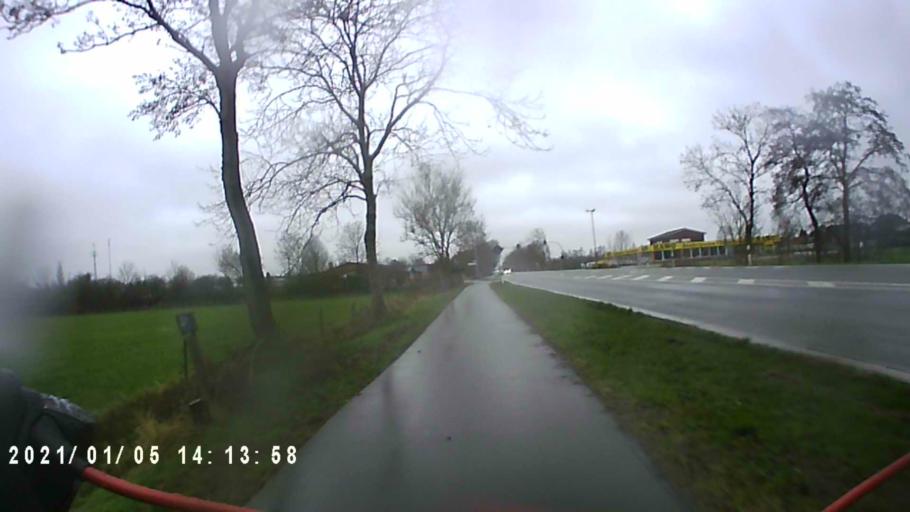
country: DE
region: Lower Saxony
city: Weener
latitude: 53.1726
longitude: 7.3200
